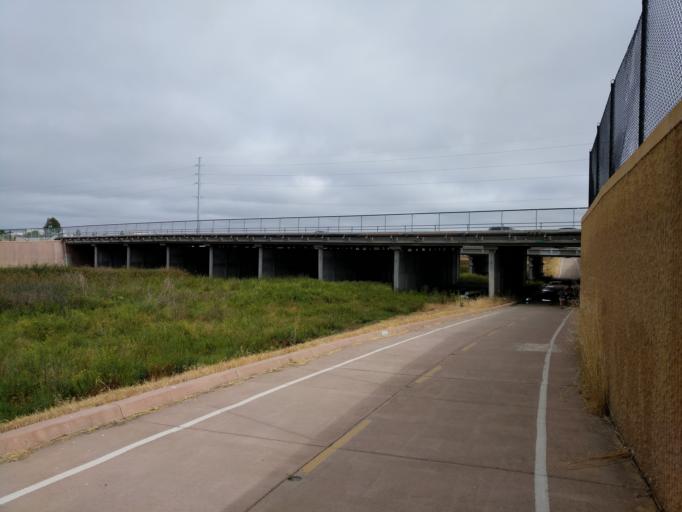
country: US
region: California
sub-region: Santa Clara County
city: Milpitas
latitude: 37.4183
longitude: -121.9673
